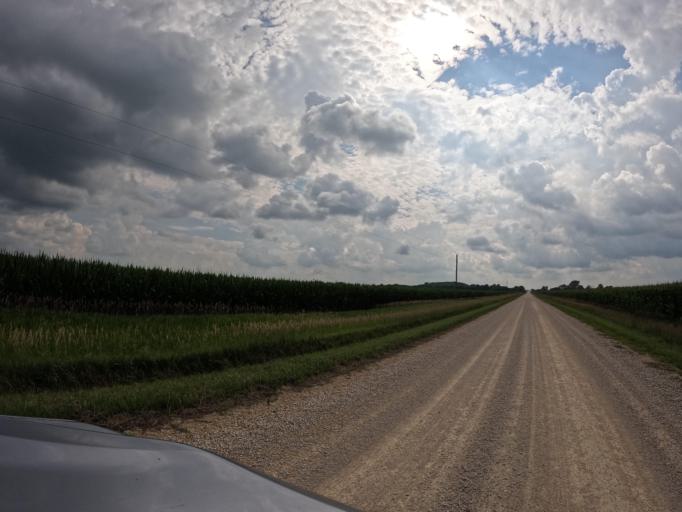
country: US
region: Iowa
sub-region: Clinton County
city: De Witt
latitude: 41.8012
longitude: -90.4045
